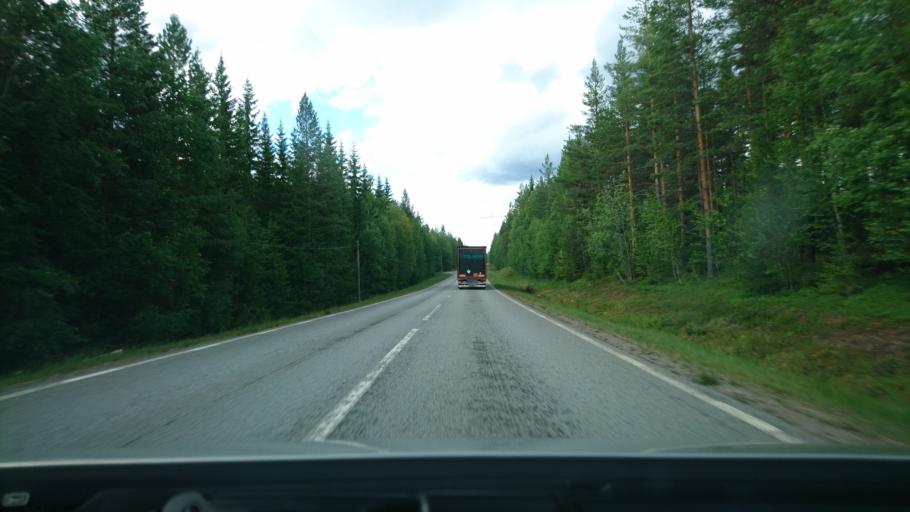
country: SE
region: Vaesterbotten
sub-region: Asele Kommun
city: Asele
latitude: 63.8486
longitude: 17.1583
